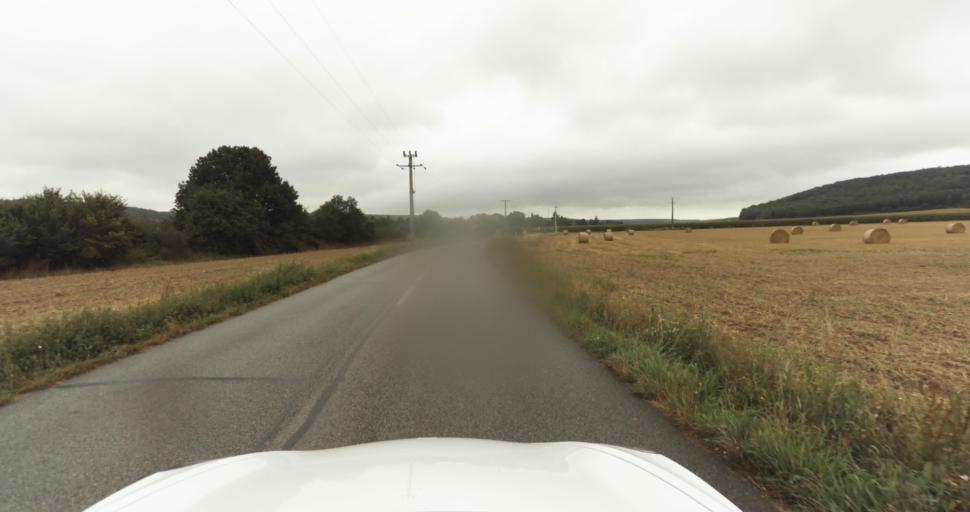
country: FR
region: Haute-Normandie
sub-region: Departement de l'Eure
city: Normanville
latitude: 49.0788
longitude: 1.1459
